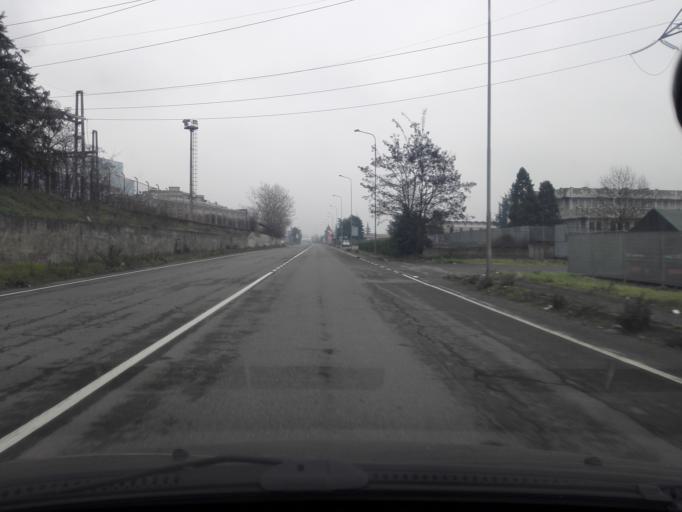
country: IT
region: Piedmont
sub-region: Provincia di Alessandria
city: Pasturana
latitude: 44.7753
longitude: 8.7604
